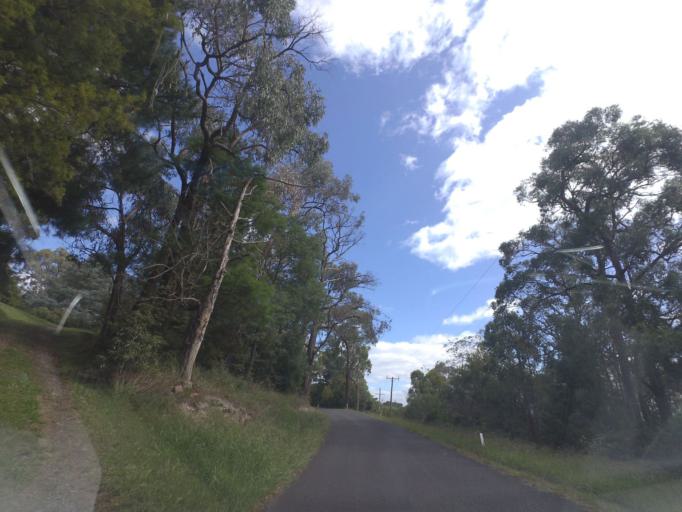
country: AU
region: Victoria
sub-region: Yarra Ranges
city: Mount Evelyn
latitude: -37.7900
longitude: 145.4098
